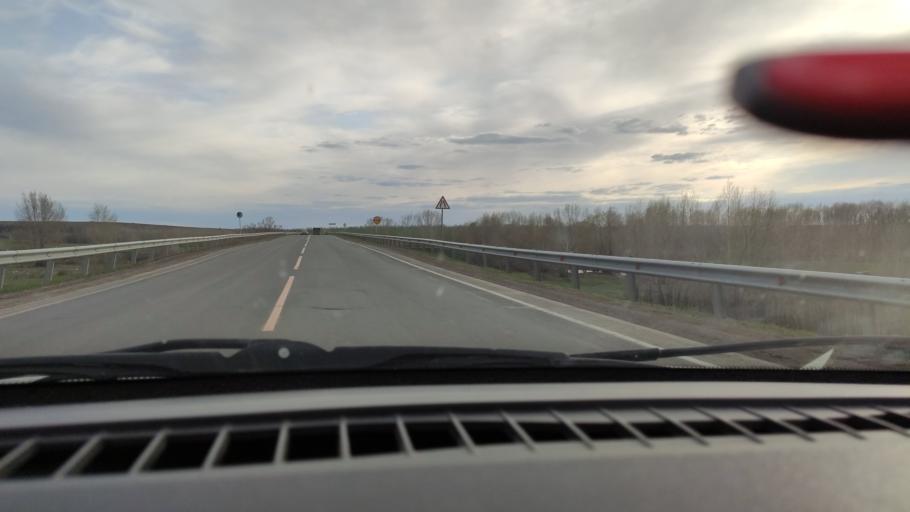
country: RU
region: Orenburg
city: Sakmara
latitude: 52.1961
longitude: 55.3074
